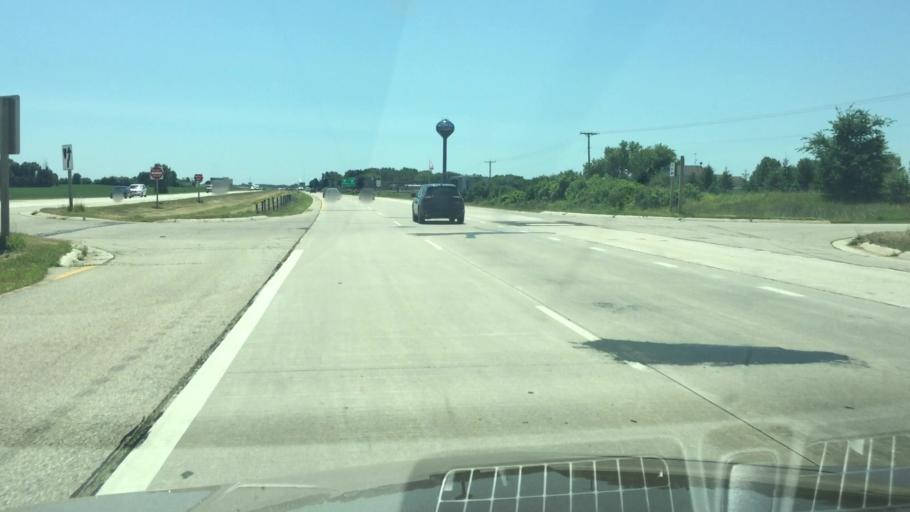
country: US
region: Wisconsin
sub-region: Dodge County
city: Beaver Dam
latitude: 43.5027
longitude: -88.8090
